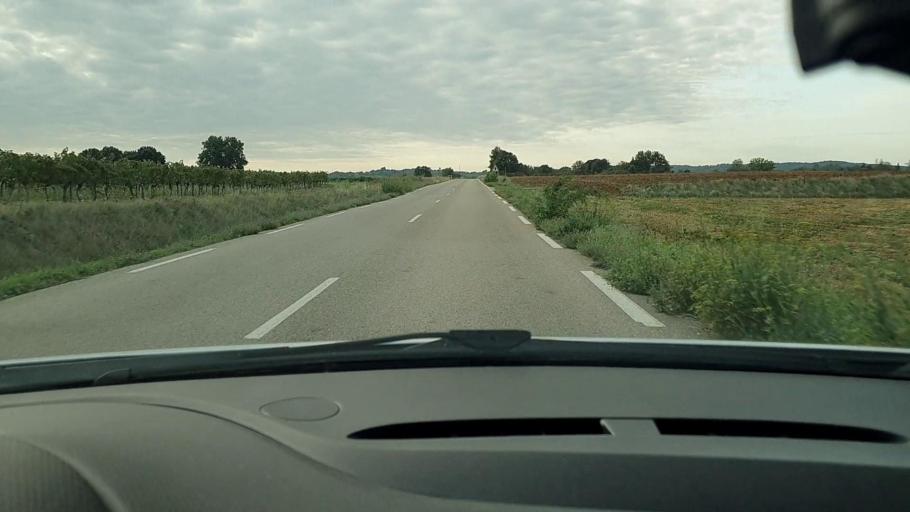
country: FR
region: Languedoc-Roussillon
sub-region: Departement du Gard
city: Mons
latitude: 44.0809
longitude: 4.2188
